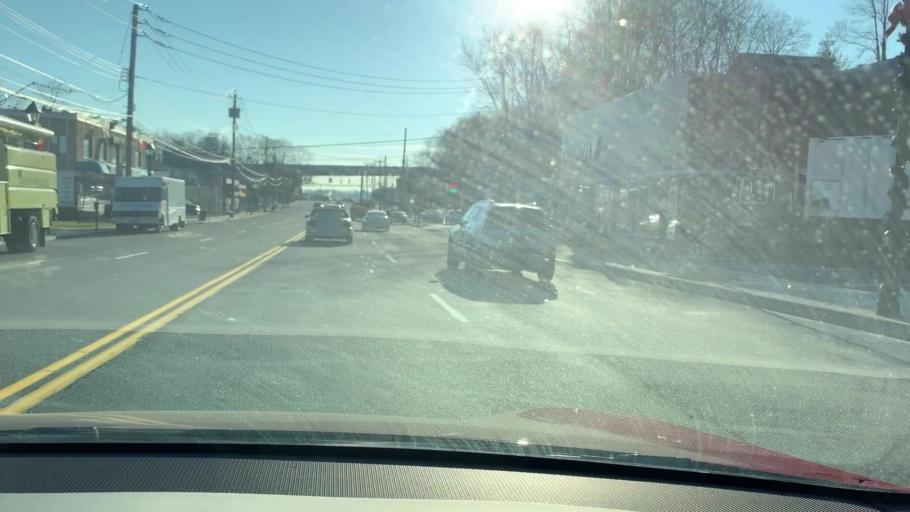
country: US
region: New York
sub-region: Westchester County
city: Elmsford
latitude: 41.0523
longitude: -73.8143
